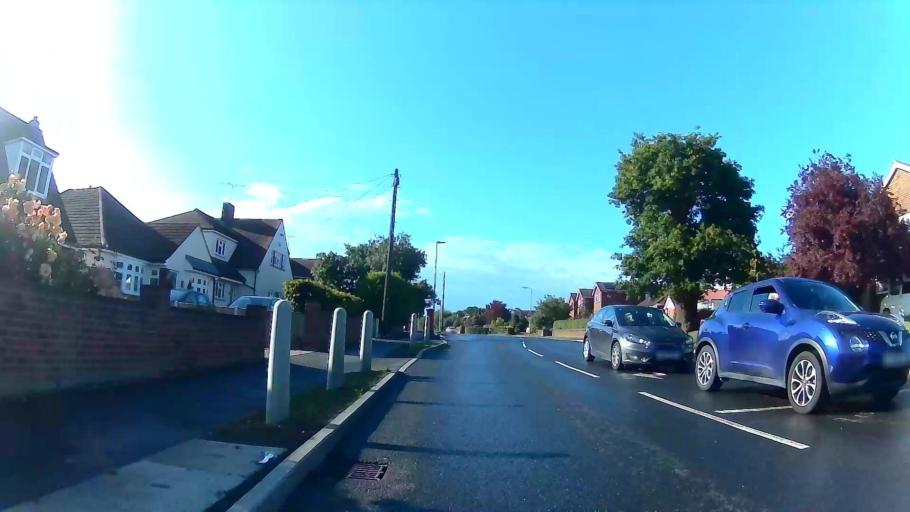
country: GB
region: England
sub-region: Essex
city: Writtle
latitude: 51.7413
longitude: 0.4451
